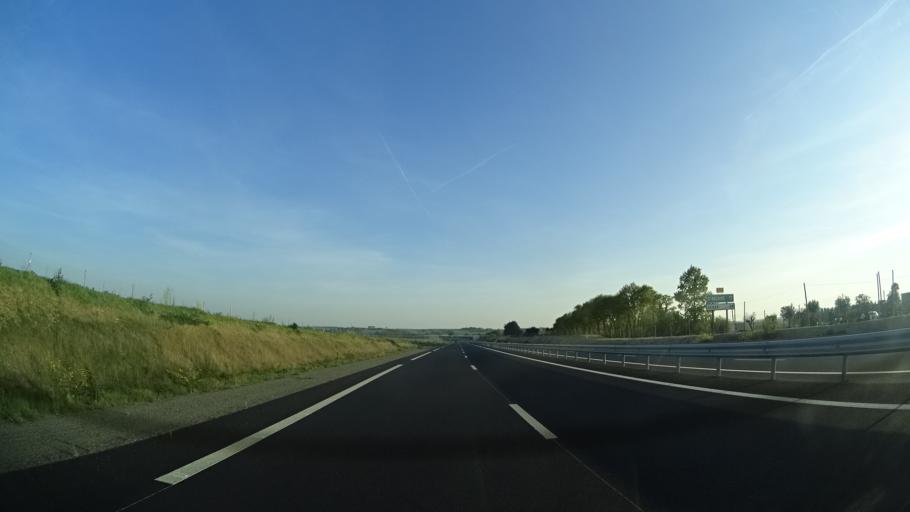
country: FR
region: Brittany
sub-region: Departement d'Ille-et-Vilaine
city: Pipriac
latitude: 47.8073
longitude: -1.9203
